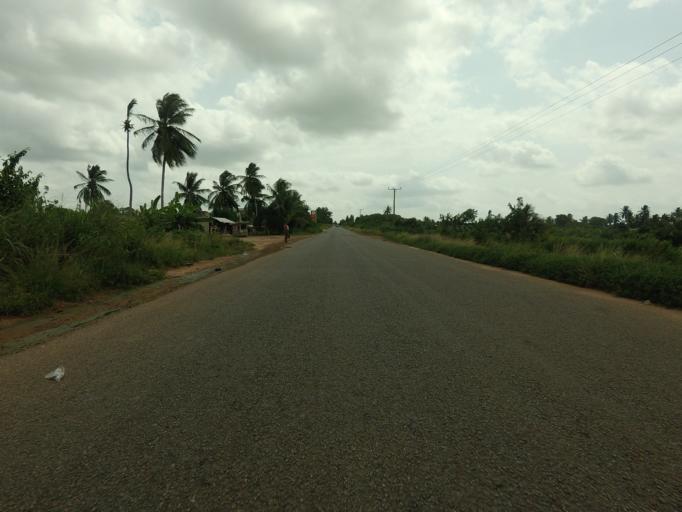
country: TG
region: Maritime
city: Lome
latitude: 6.1717
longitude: 1.0776
